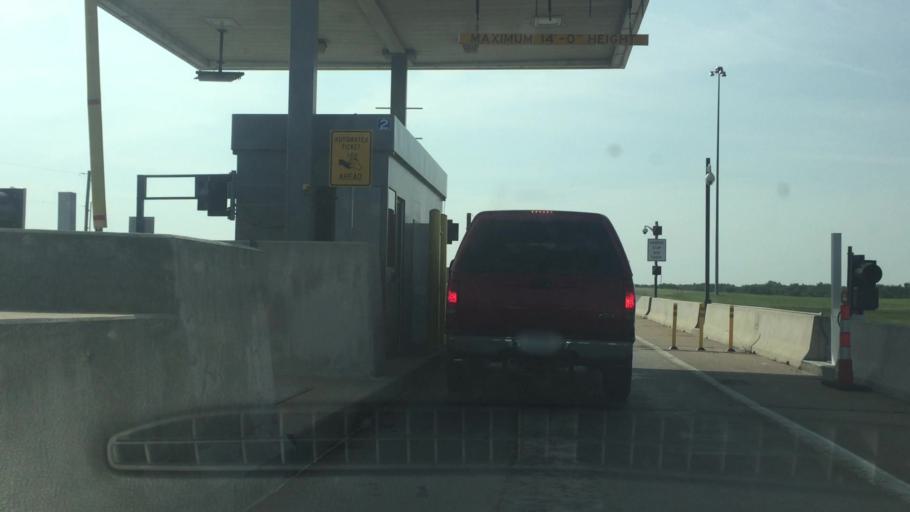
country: US
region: Kansas
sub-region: Butler County
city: Andover
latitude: 37.6889
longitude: -97.1826
